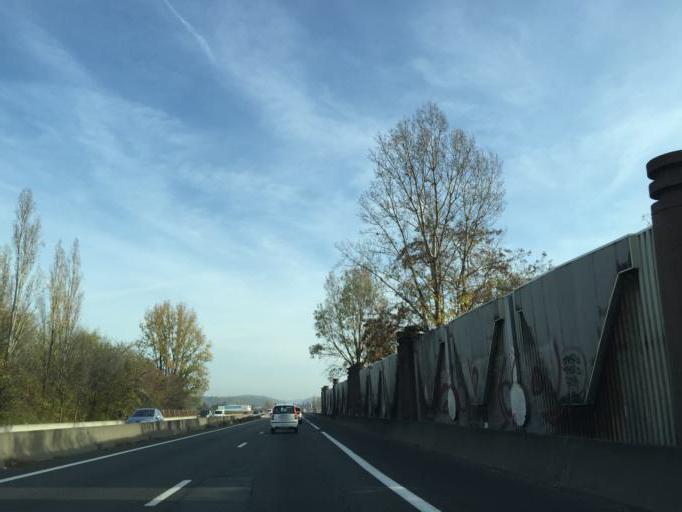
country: FR
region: Rhone-Alpes
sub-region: Departement de la Loire
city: La Grand-Croix
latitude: 45.4970
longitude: 4.5579
